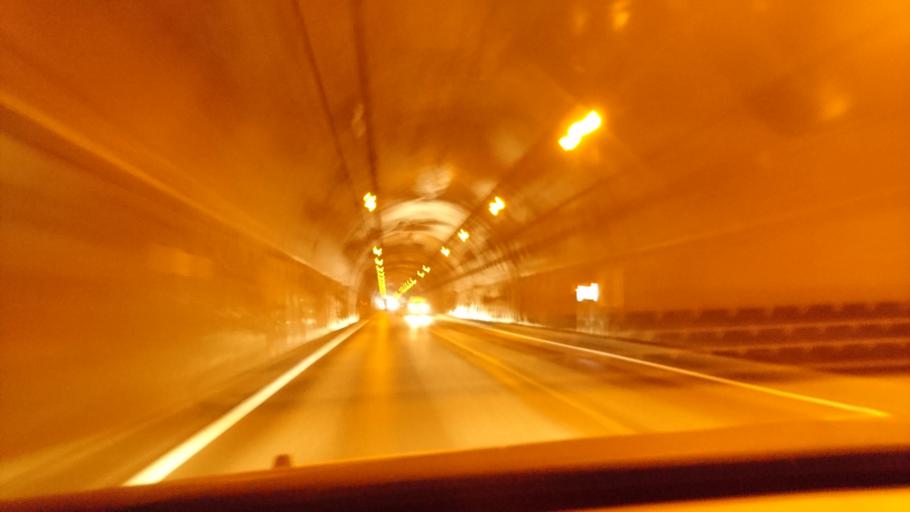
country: JP
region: Iwate
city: Miyako
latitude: 39.7203
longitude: 141.9674
